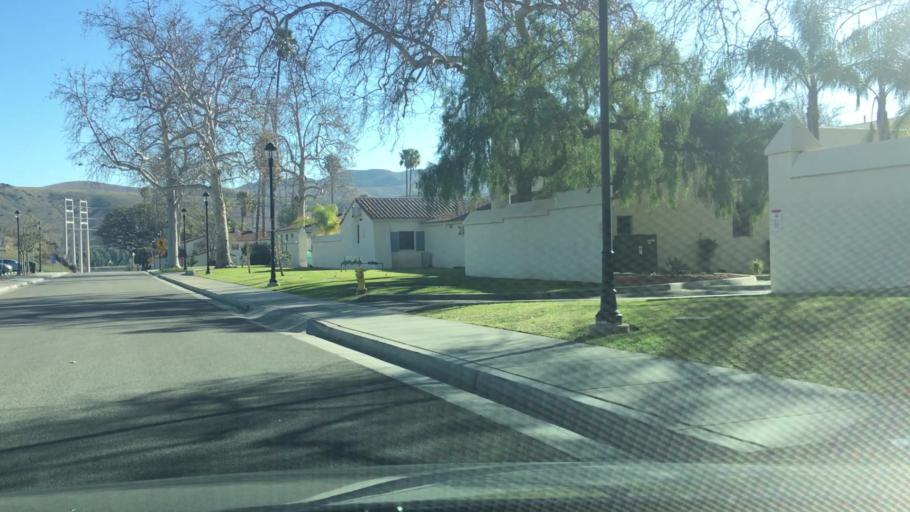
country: US
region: California
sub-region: Ventura County
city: Camarillo
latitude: 34.1612
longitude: -119.0417
